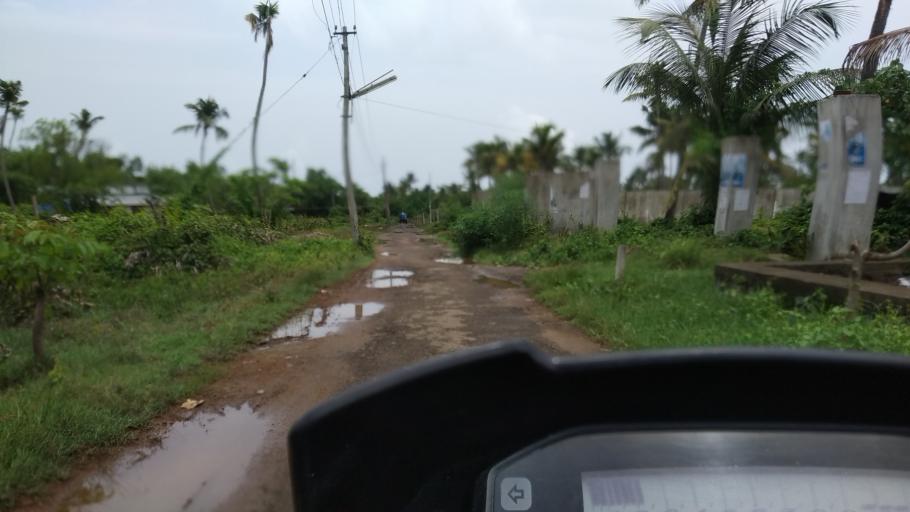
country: IN
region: Kerala
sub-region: Ernakulam
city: Elur
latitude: 10.0649
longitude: 76.2071
